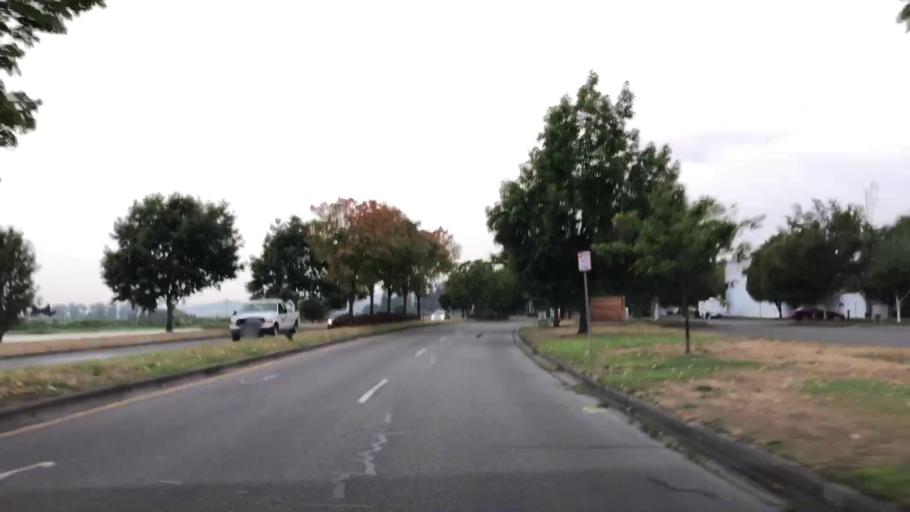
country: US
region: Washington
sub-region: Snohomish County
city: Monroe
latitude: 47.8666
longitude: -122.0095
